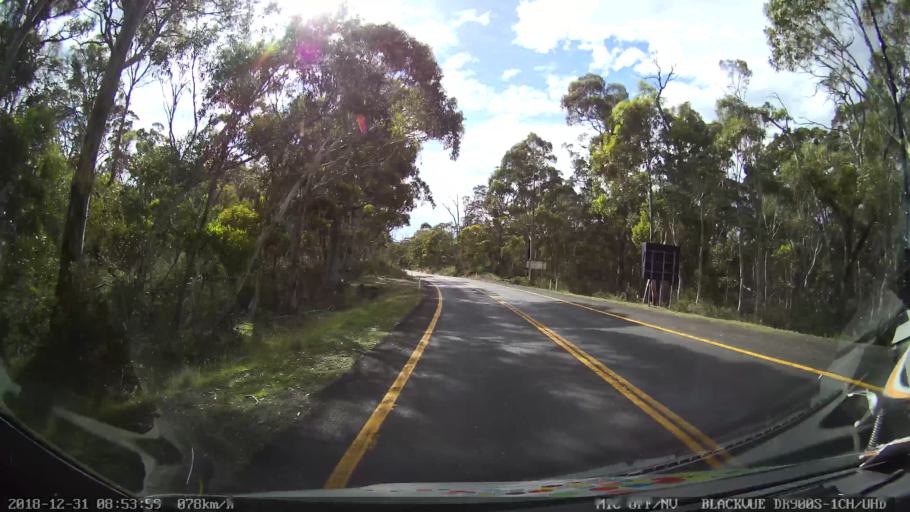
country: AU
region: New South Wales
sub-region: Snowy River
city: Jindabyne
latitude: -36.3522
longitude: 148.5549
